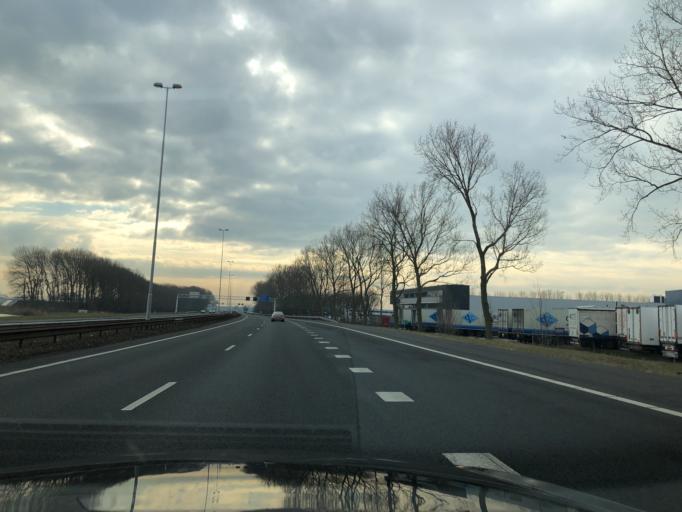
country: NL
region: South Holland
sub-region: Gemeente Westland
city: Maasdijk
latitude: 51.9479
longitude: 4.2346
